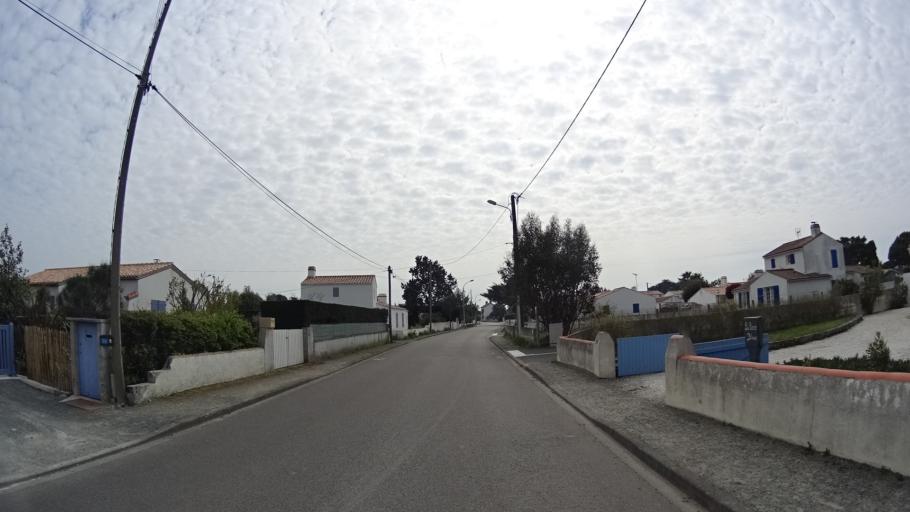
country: FR
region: Pays de la Loire
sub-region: Departement de la Vendee
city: La Gueriniere
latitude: 47.0078
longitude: -2.2360
